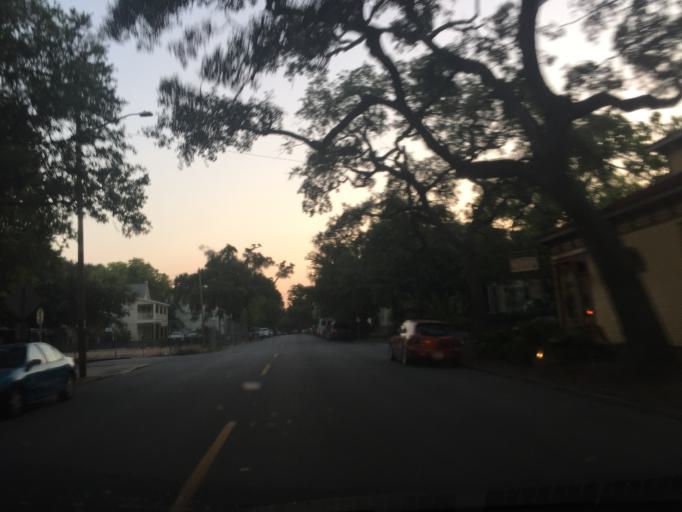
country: US
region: Georgia
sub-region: Chatham County
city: Savannah
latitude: 32.0667
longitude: -81.0918
